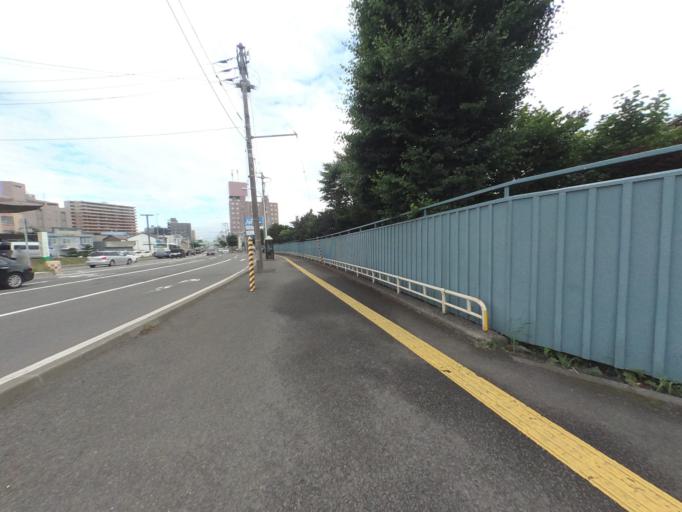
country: JP
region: Hokkaido
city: Sapporo
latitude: 43.0645
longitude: 141.3805
